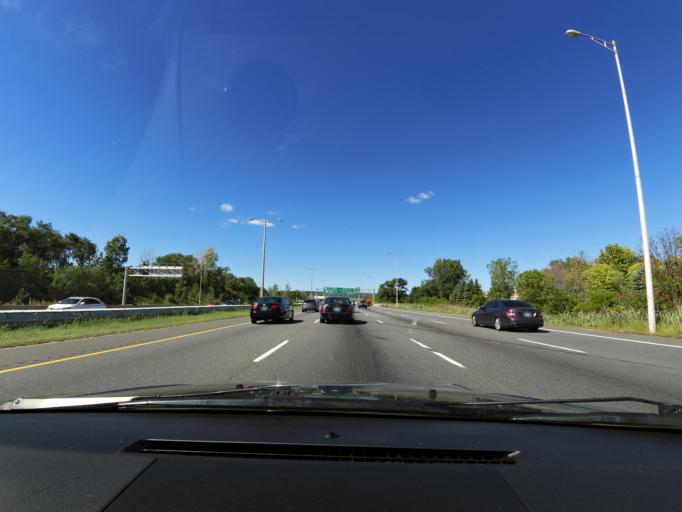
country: CA
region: Ontario
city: Burlington
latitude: 43.3212
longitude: -79.8169
